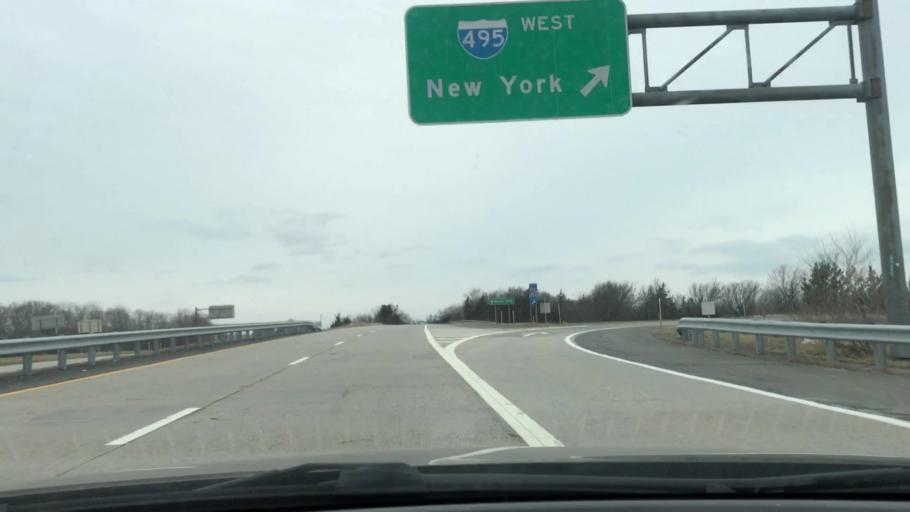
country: US
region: New York
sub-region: Suffolk County
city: Calverton
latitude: 40.9212
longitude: -72.7244
